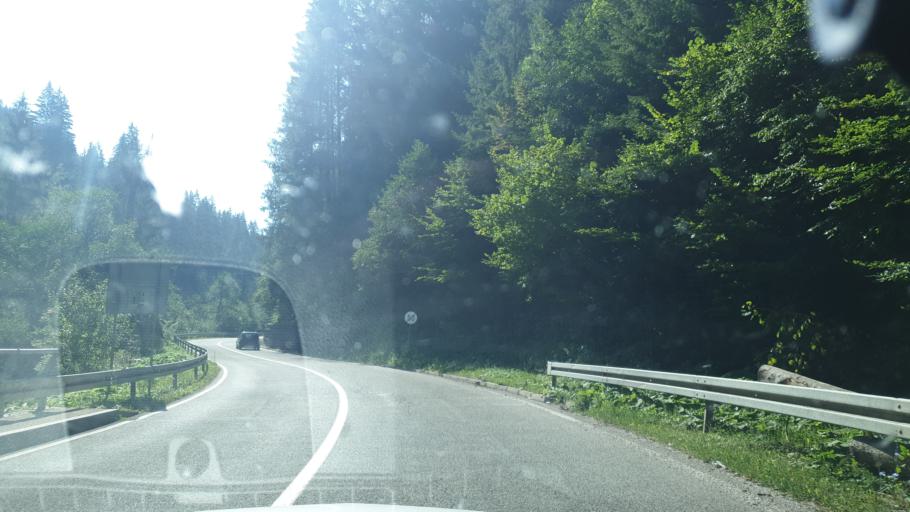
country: RS
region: Central Serbia
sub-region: Zlatiborski Okrug
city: Nova Varos
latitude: 43.4799
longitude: 19.8303
